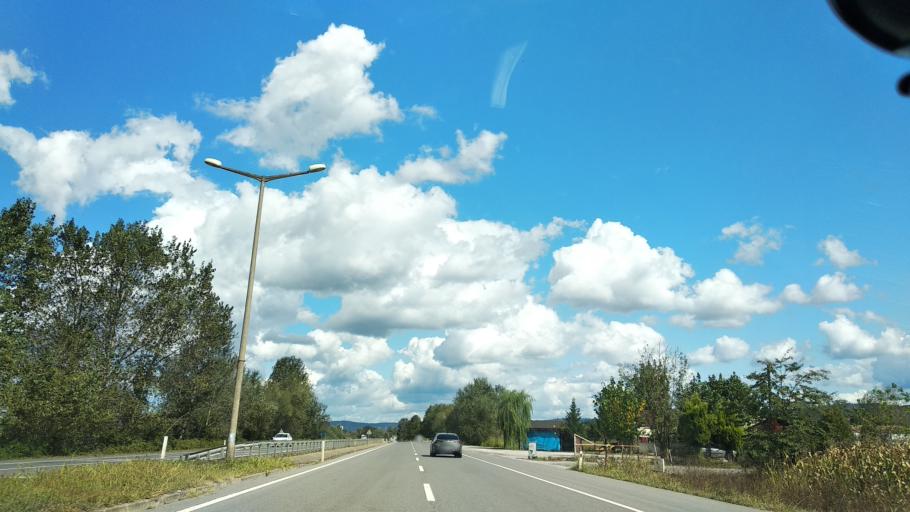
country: TR
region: Sakarya
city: Ferizli
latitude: 40.9810
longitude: 30.5327
